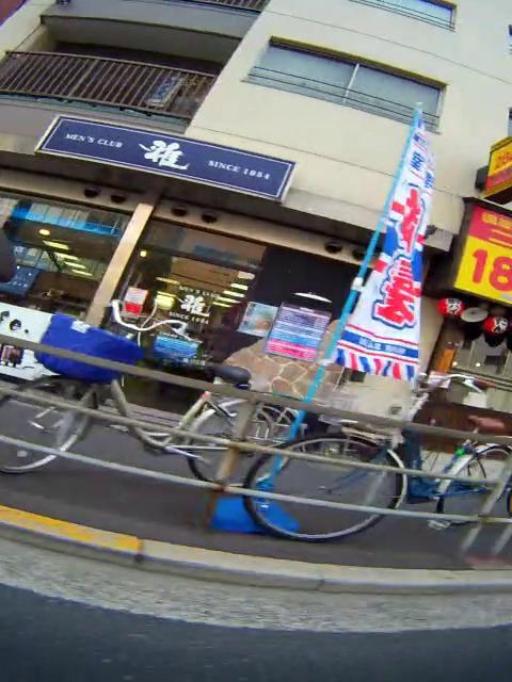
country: JP
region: Osaka
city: Osaka-shi
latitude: 34.6801
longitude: 135.5445
